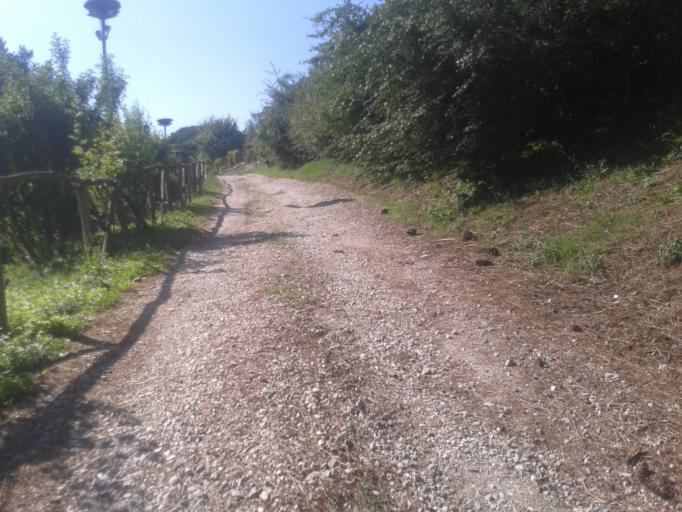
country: IT
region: Campania
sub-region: Provincia di Napoli
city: Pompei
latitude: 40.7525
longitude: 14.4953
